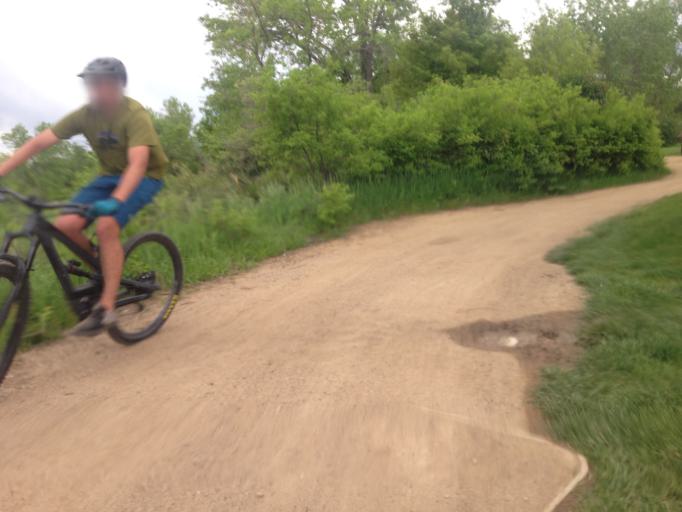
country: US
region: Colorado
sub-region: Boulder County
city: Boulder
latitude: 40.0312
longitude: -105.2337
